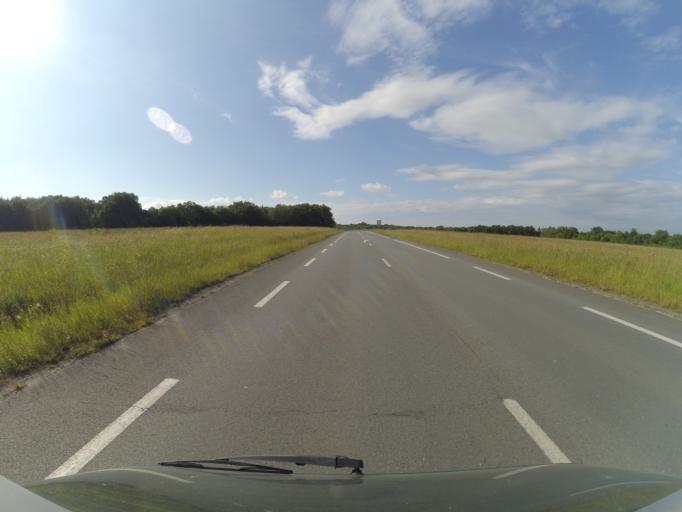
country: FR
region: Poitou-Charentes
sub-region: Departement de la Charente-Maritime
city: Saint-Agnant
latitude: 45.8312
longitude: -0.9376
